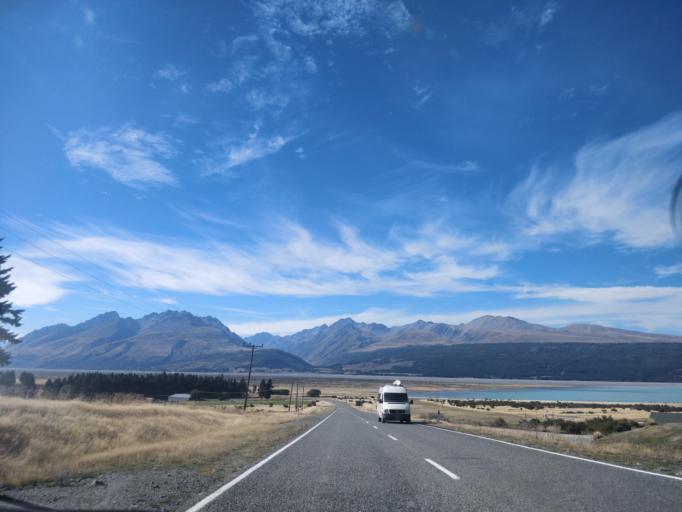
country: NZ
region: Canterbury
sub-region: Timaru District
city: Pleasant Point
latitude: -43.9119
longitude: 170.1203
